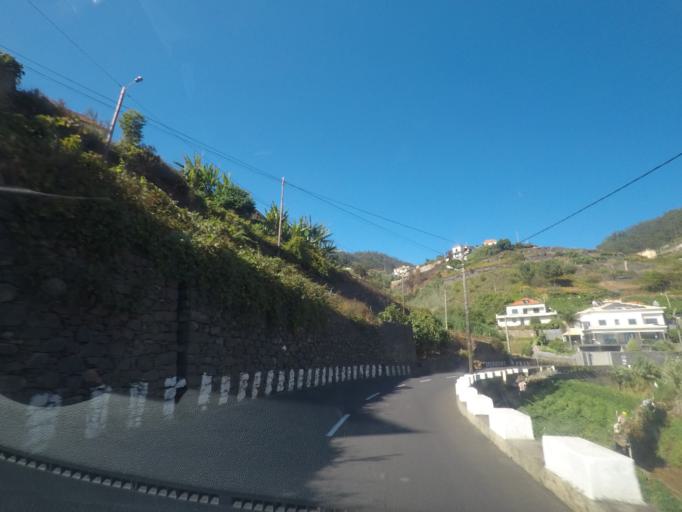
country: PT
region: Madeira
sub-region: Ribeira Brava
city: Campanario
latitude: 32.6749
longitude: -17.0251
